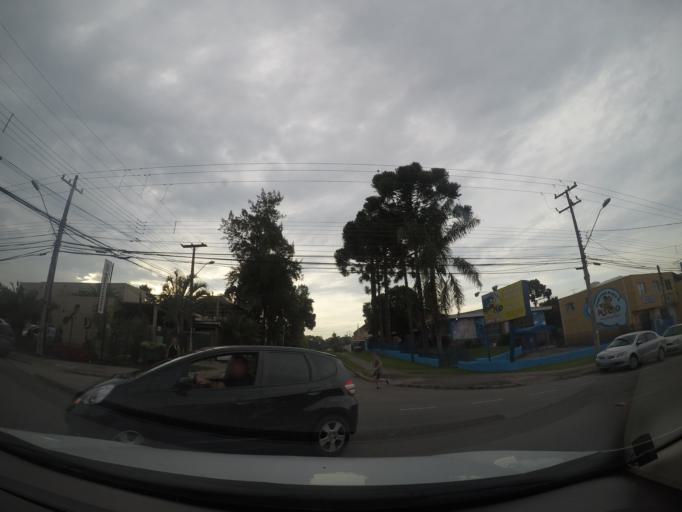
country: BR
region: Parana
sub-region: Sao Jose Dos Pinhais
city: Sao Jose dos Pinhais
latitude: -25.5132
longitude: -49.2401
